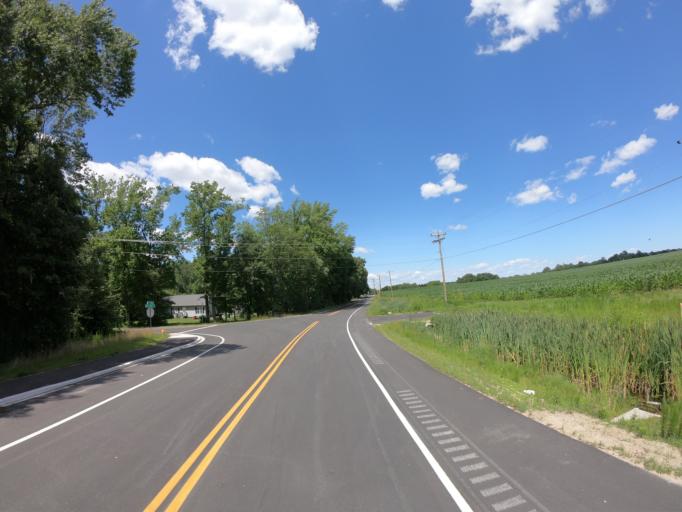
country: US
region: Delaware
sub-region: Sussex County
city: Milford
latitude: 38.9303
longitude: -75.4089
